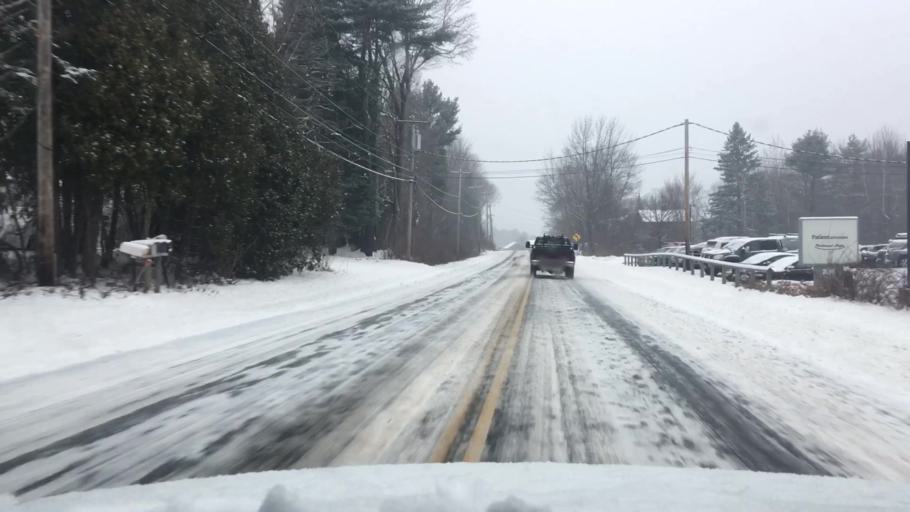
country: US
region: Maine
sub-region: Cumberland County
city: Cumberland Center
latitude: 43.8518
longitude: -70.3215
